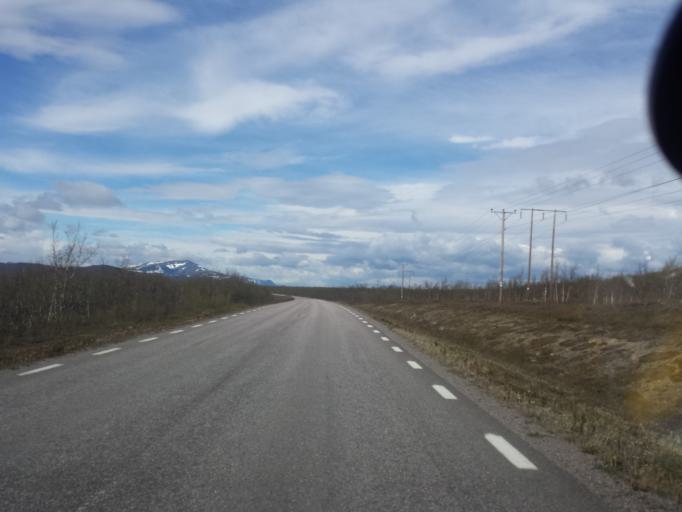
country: SE
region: Norrbotten
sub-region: Kiruna Kommun
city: Kiruna
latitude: 68.0483
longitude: 19.8305
